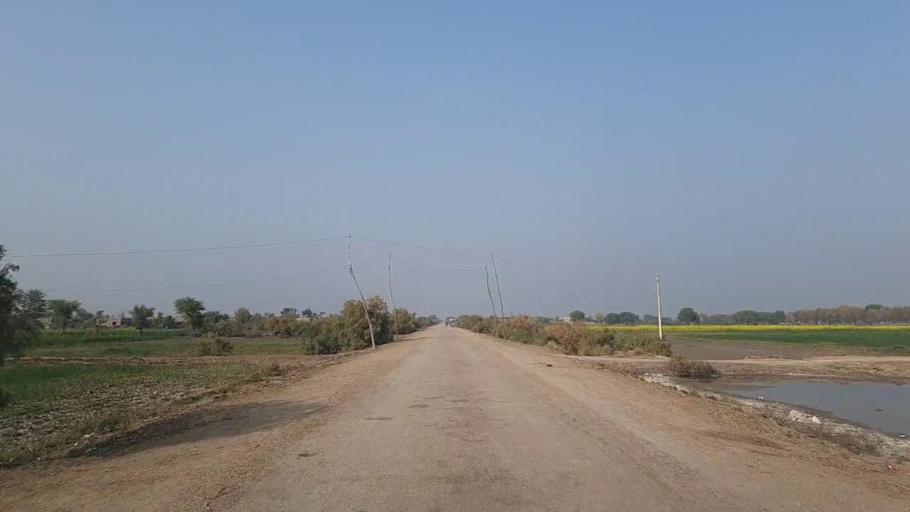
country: PK
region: Sindh
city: Nawabshah
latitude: 26.3332
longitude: 68.4891
